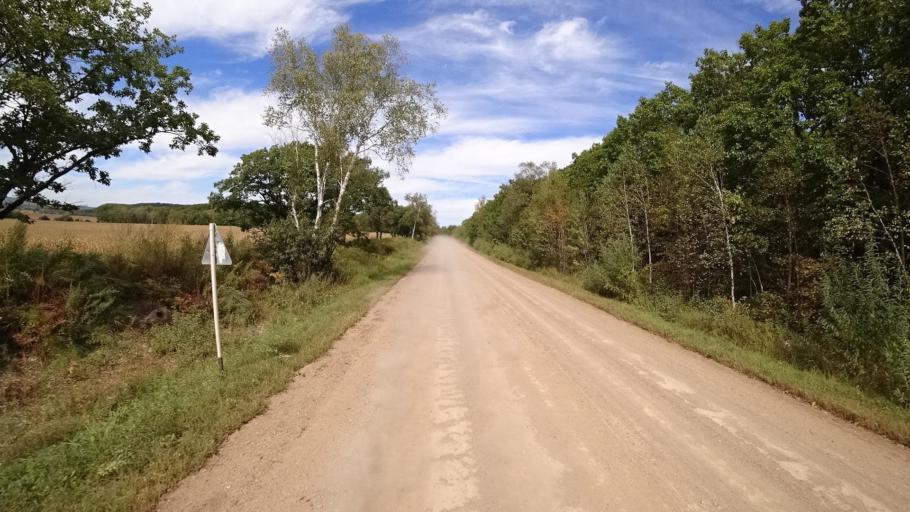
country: RU
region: Primorskiy
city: Yakovlevka
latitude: 44.5937
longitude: 133.6061
